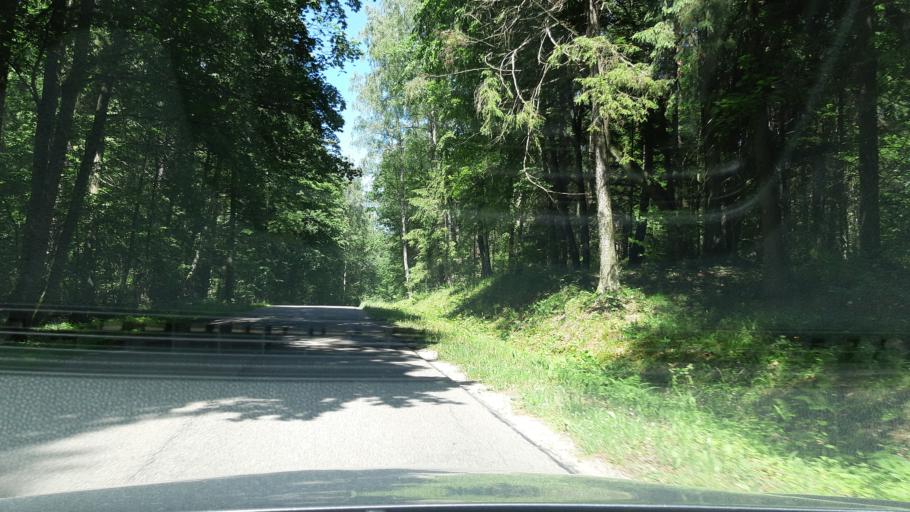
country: PL
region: Warmian-Masurian Voivodeship
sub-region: Powiat mragowski
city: Mikolajki
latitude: 53.7485
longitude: 21.5036
